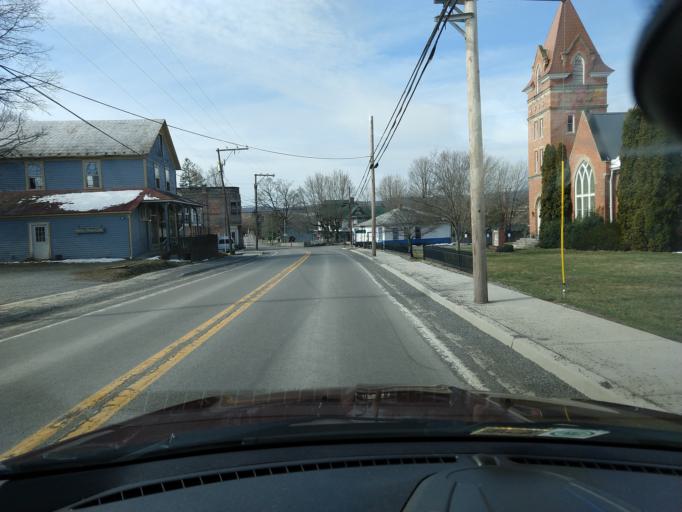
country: US
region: West Virginia
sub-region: Pocahontas County
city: Marlinton
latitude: 38.1358
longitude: -80.2124
